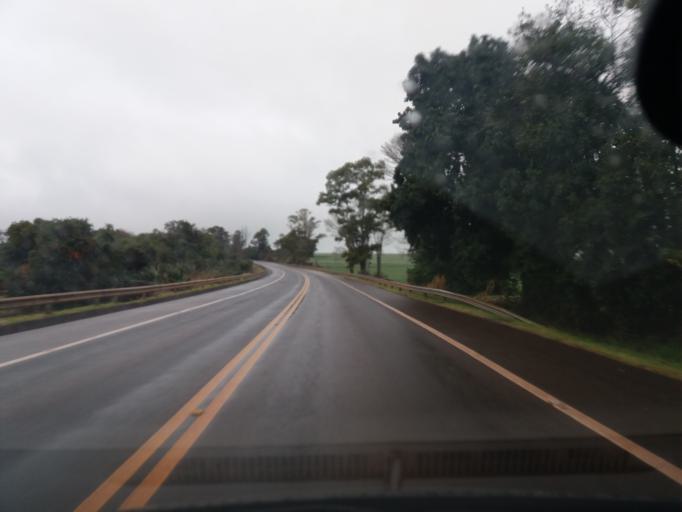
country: BR
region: Parana
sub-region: Campo Mourao
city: Campo Mourao
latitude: -24.3193
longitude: -52.6283
